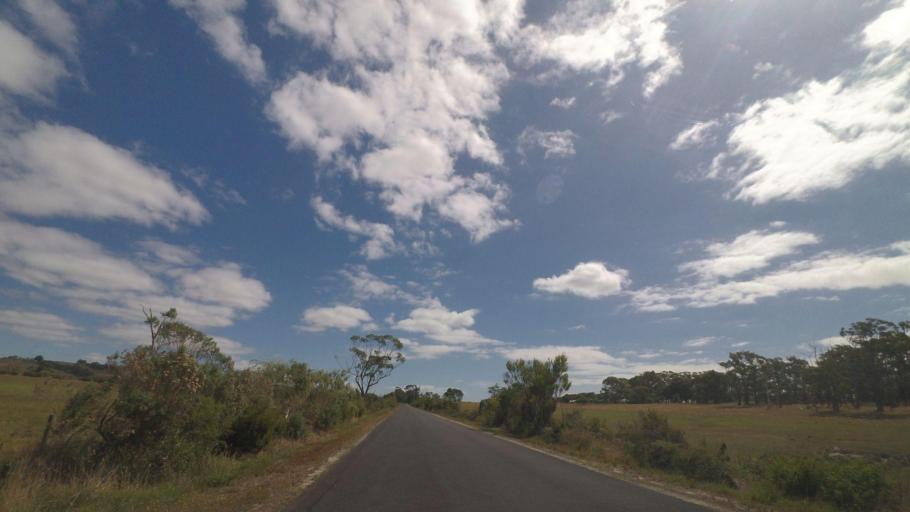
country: AU
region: Victoria
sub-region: Cardinia
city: Bunyip
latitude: -38.3166
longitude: 145.7367
